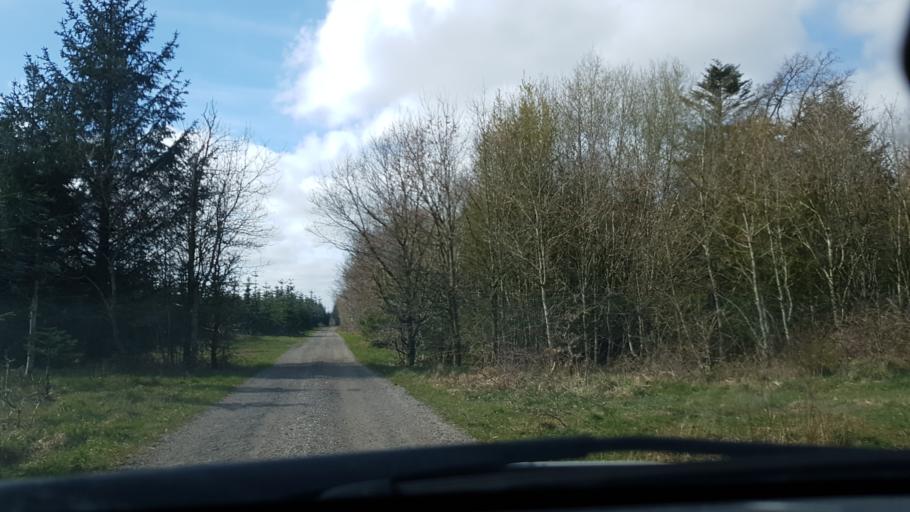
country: DK
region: South Denmark
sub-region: Haderslev Kommune
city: Gram
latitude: 55.2997
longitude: 8.9780
